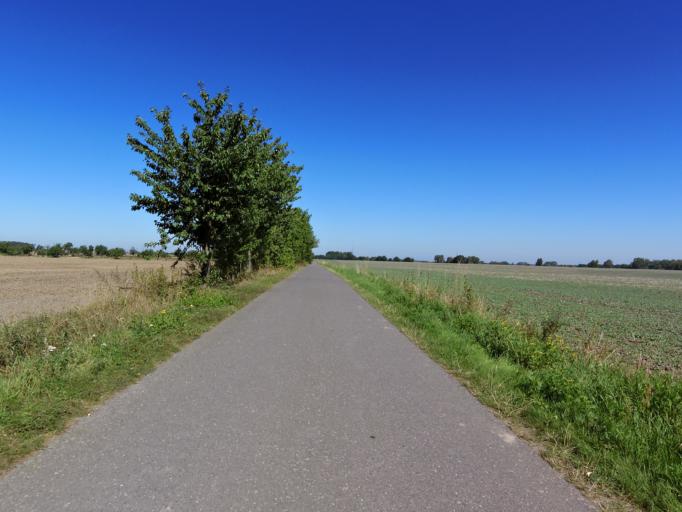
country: DE
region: Saxony
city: Dommitzsch
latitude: 51.6436
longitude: 12.8587
